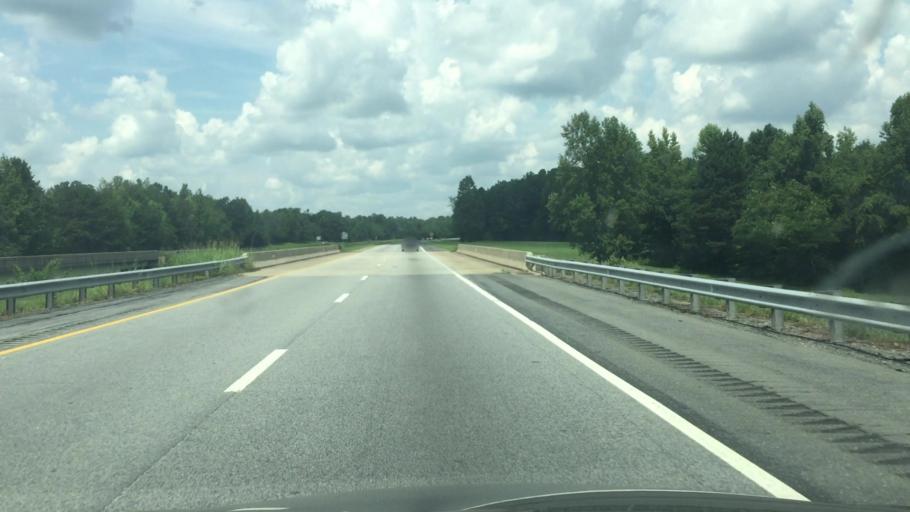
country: US
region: North Carolina
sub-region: Guilford County
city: Pleasant Garden
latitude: 35.9220
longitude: -79.8251
